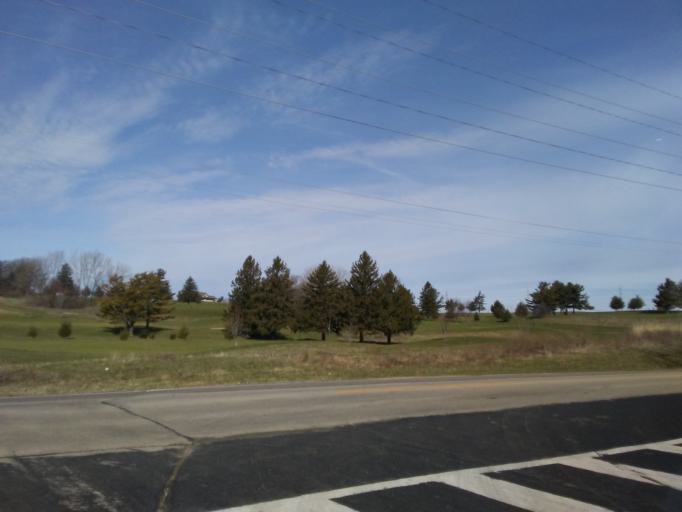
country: US
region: Wisconsin
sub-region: Dane County
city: Middleton
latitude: 43.0854
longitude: -89.5365
